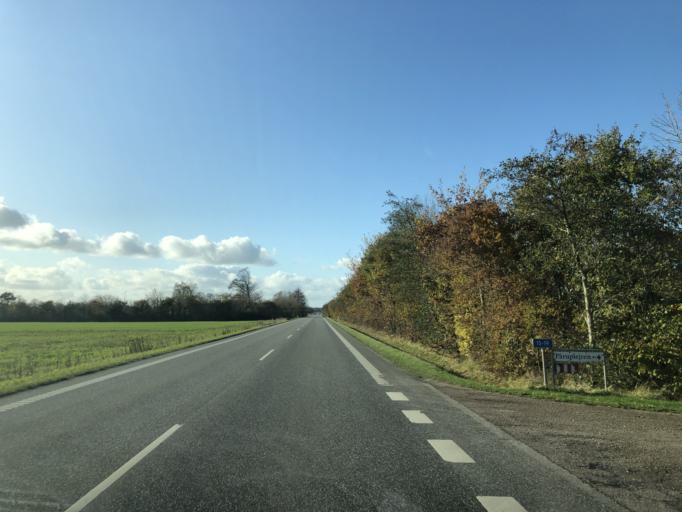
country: DK
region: Central Jutland
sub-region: Ikast-Brande Kommune
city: Bording Kirkeby
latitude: 56.1374
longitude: 9.3676
